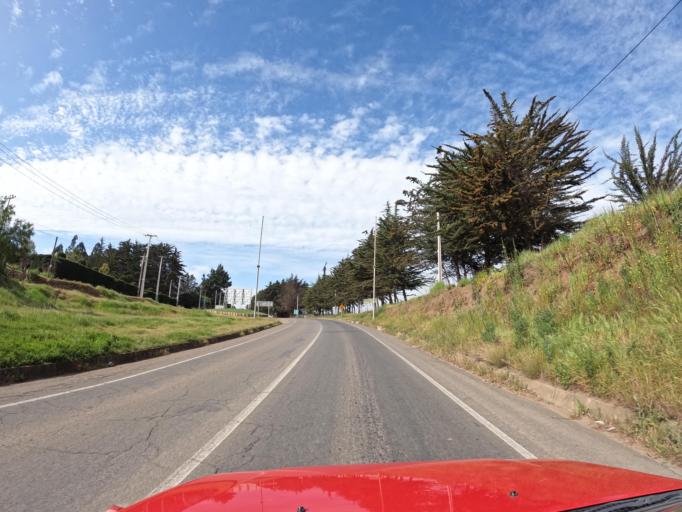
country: CL
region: O'Higgins
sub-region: Provincia de Colchagua
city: Santa Cruz
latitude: -34.3819
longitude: -71.9745
